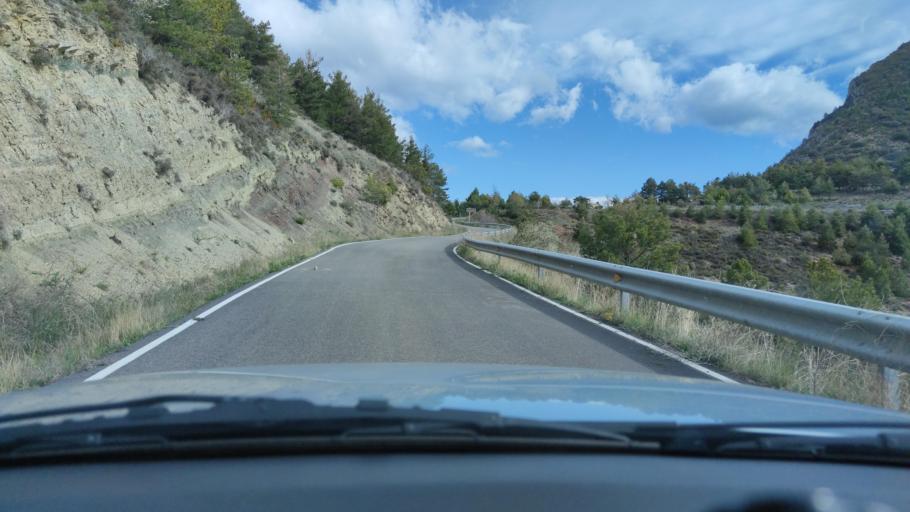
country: ES
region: Catalonia
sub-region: Provincia de Lleida
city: Alas i Cerc
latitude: 42.2525
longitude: 1.4897
